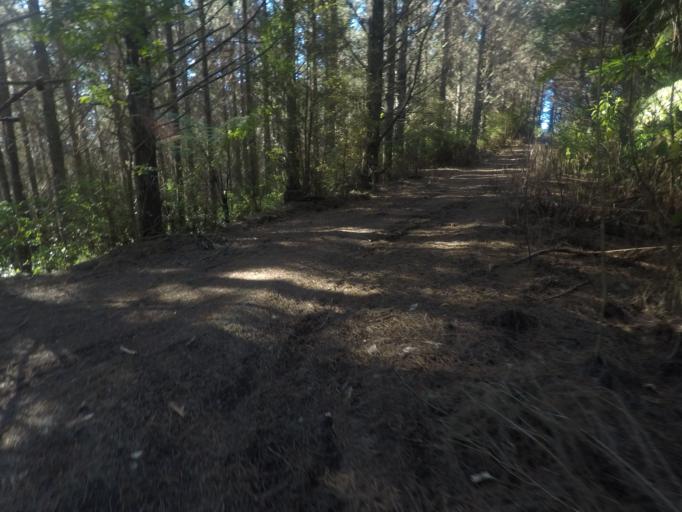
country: NZ
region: Auckland
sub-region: Auckland
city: Muriwai Beach
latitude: -36.7461
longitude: 174.5559
